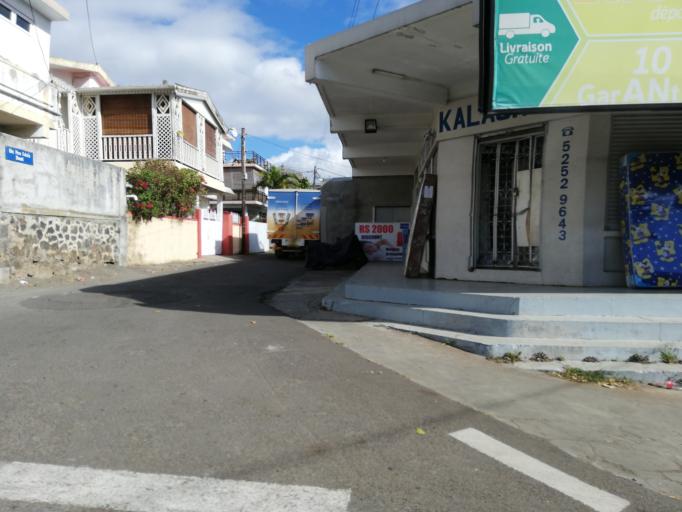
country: MU
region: Plaines Wilhems
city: Ebene
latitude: -20.2313
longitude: 57.4585
